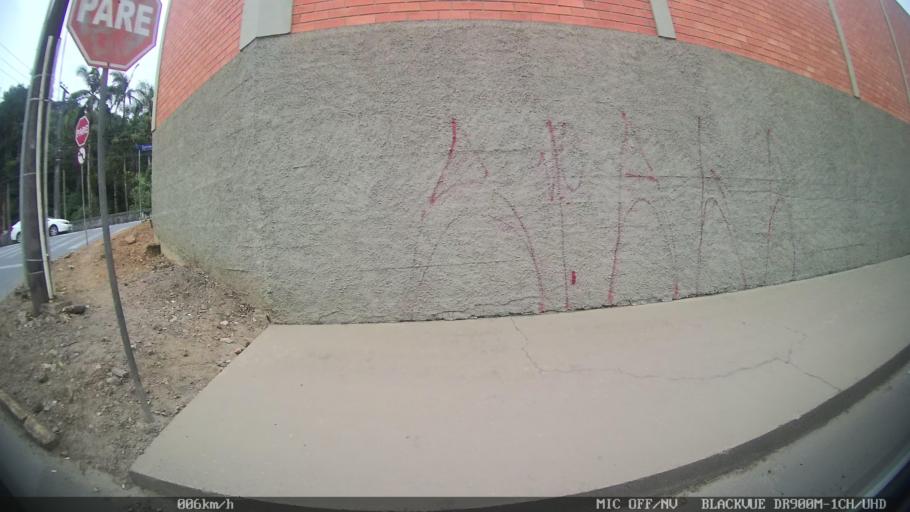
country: BR
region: Santa Catarina
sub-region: Joinville
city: Joinville
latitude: -26.3430
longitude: -48.8474
